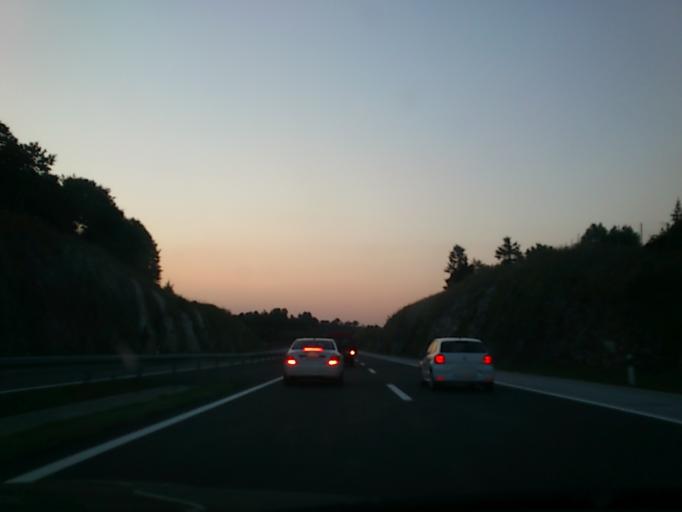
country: HR
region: Karlovacka
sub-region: Grad Ogulin
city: Ogulin
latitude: 45.3262
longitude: 15.2808
